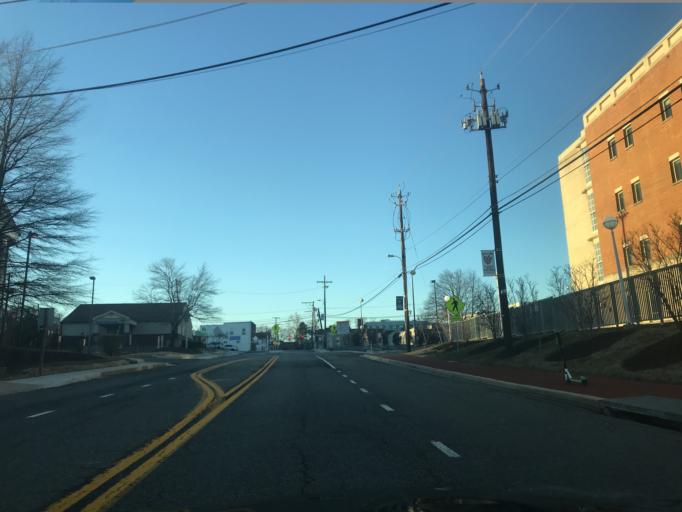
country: US
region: Maryland
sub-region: Prince George's County
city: Upper Marlboro
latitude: 38.8147
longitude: -76.7509
